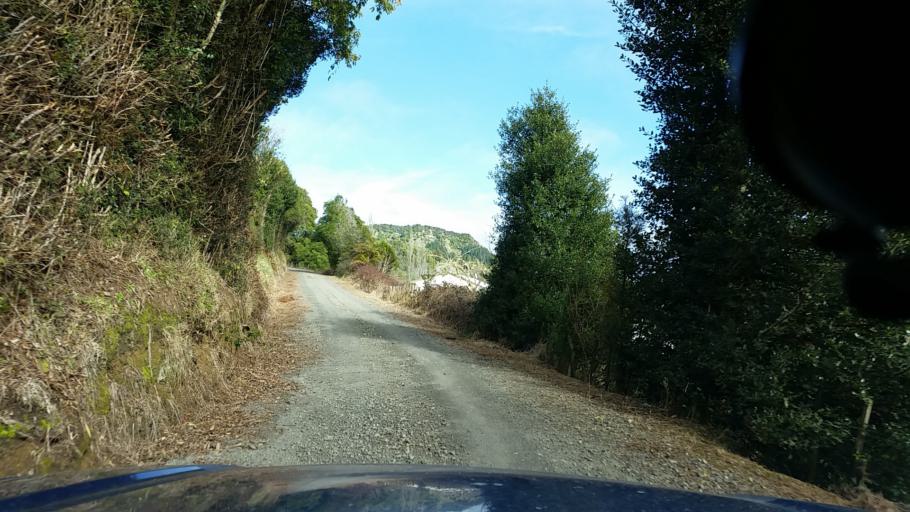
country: NZ
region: Taranaki
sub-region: New Plymouth District
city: Waitara
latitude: -39.0323
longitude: 174.8011
